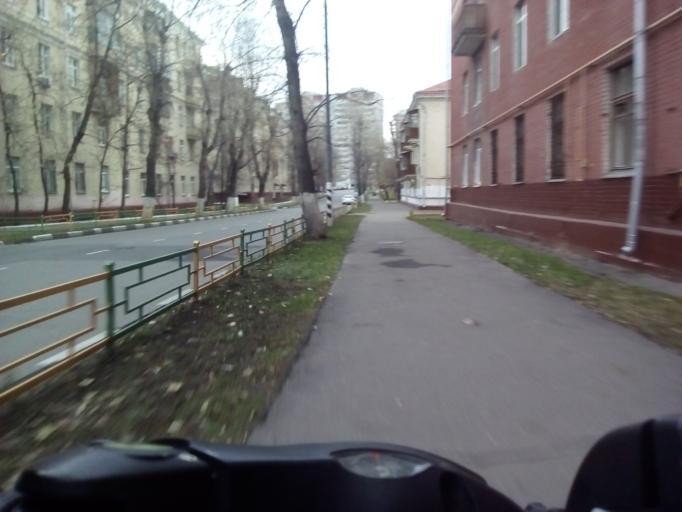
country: RU
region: Moscow
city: Lefortovo
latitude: 55.7684
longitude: 37.7143
